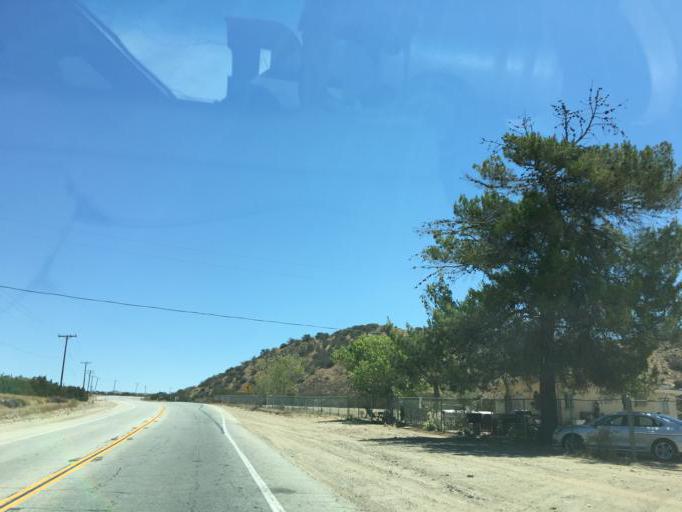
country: US
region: California
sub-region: Los Angeles County
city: Agua Dulce
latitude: 34.5220
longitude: -118.2539
